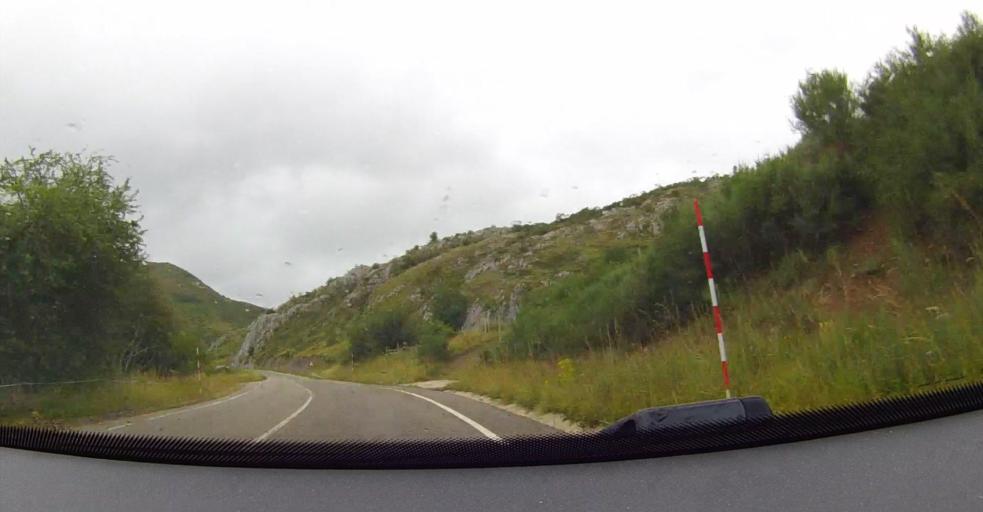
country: ES
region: Castille and Leon
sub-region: Provincia de Leon
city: Acebedo
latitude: 43.0679
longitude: -5.1411
